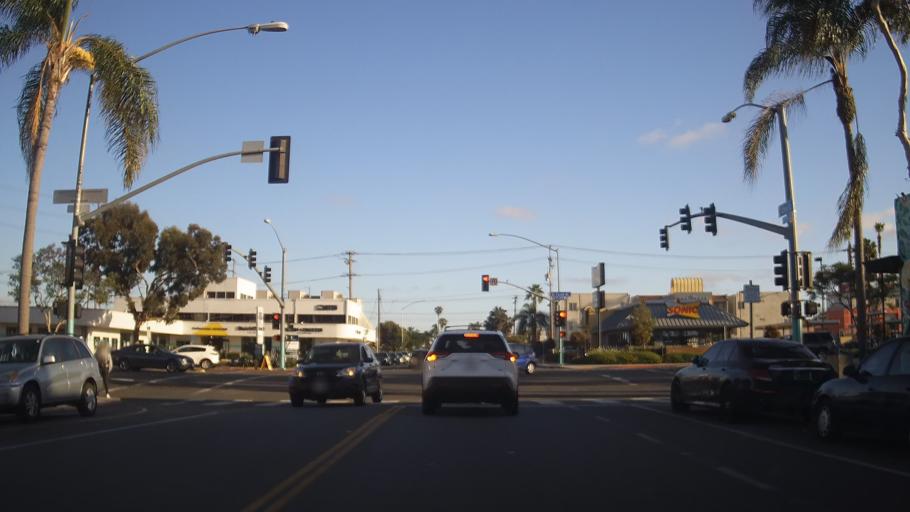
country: US
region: California
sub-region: San Diego County
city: San Diego
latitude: 32.7557
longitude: -117.1327
